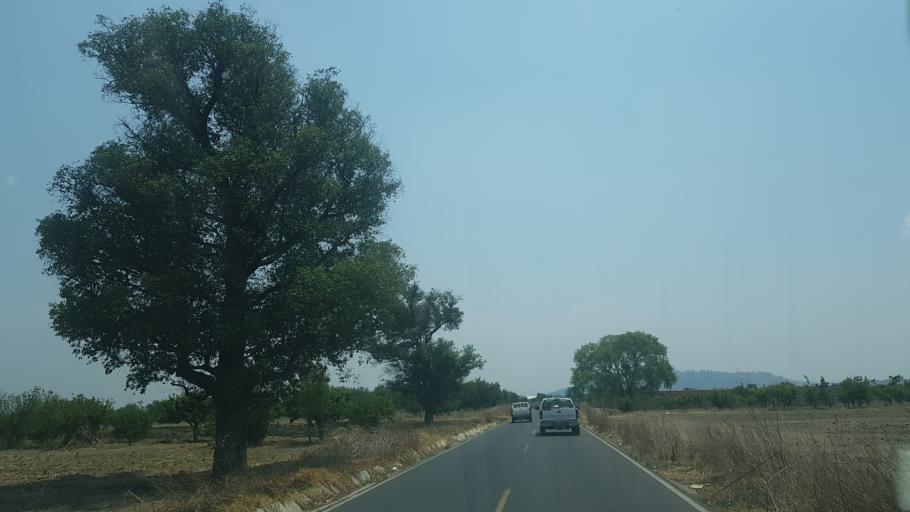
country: MX
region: Puebla
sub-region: San Jeronimo Tecuanipan
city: San Miguel Papaxtla
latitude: 19.0931
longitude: -98.3960
